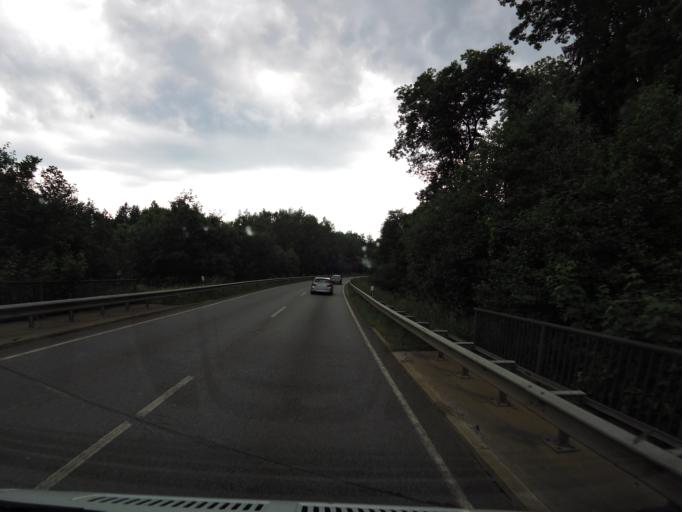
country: DE
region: Bavaria
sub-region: Lower Bavaria
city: Aicha vorm Wald
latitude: 48.6809
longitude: 13.3049
